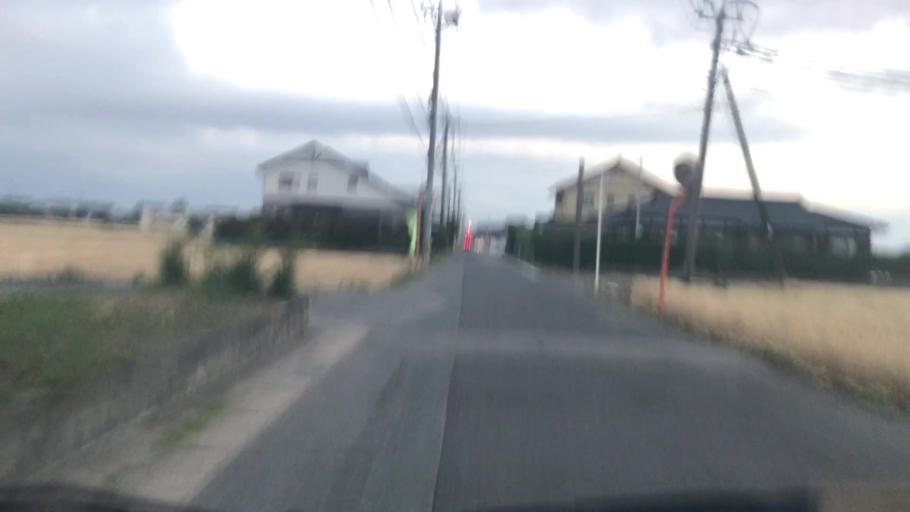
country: JP
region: Saga Prefecture
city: Saga-shi
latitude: 33.2303
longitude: 130.3019
